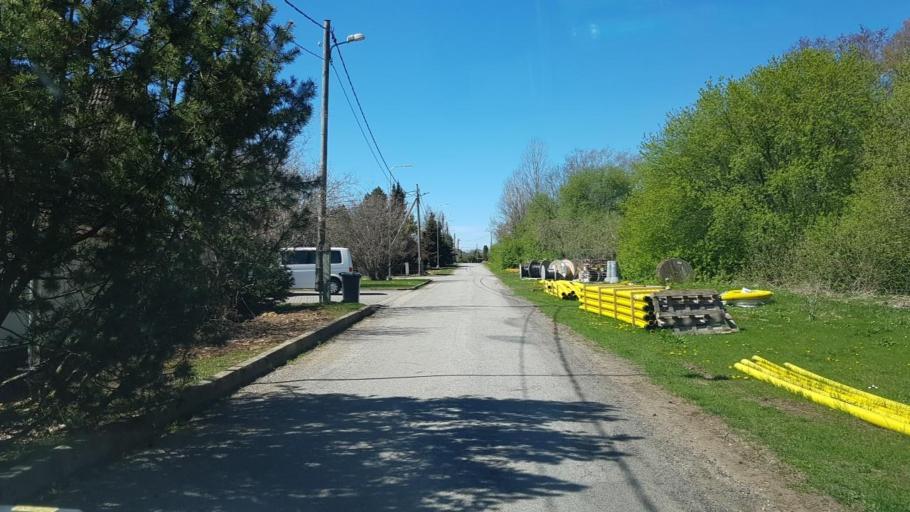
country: EE
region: Harju
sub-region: Viimsi vald
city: Viimsi
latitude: 59.4952
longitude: 24.8598
